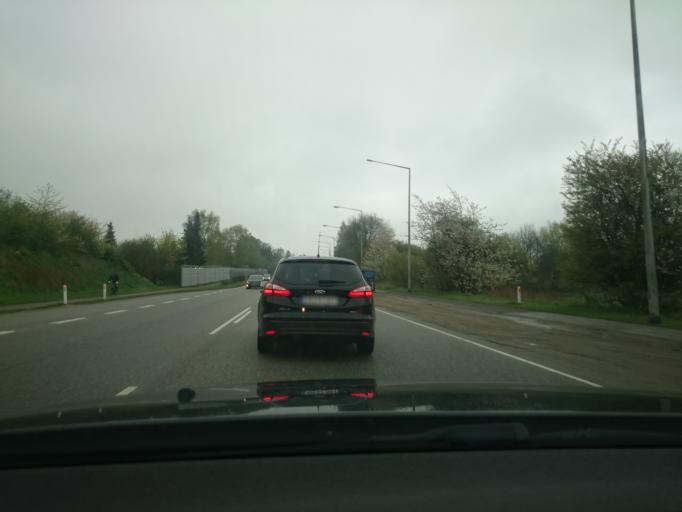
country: DK
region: Capital Region
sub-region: Herlev Kommune
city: Herlev
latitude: 55.7522
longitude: 12.4062
